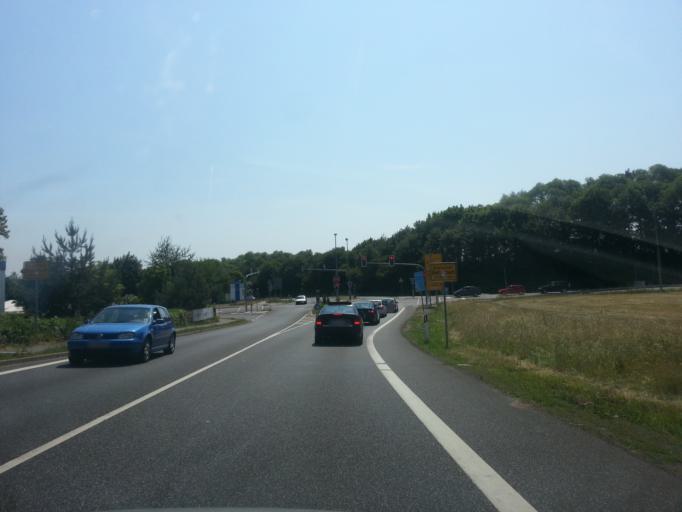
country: DE
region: Hesse
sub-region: Regierungsbezirk Darmstadt
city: Dietzenbach
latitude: 50.0013
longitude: 8.7716
